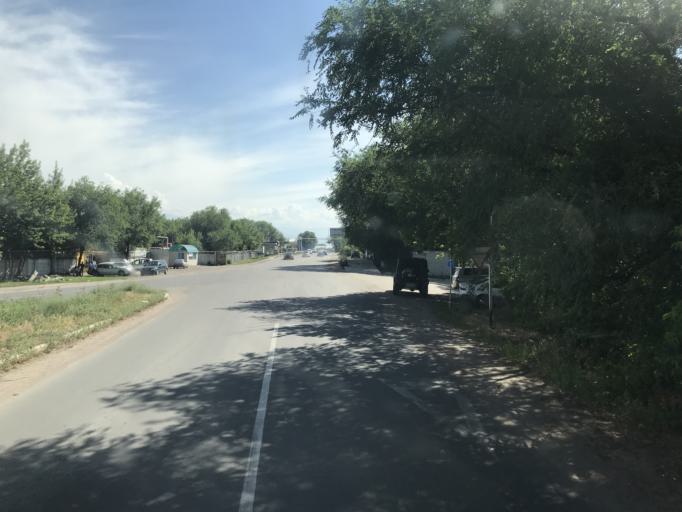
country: KZ
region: Almaty Oblysy
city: Pervomayskiy
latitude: 43.3503
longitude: 76.9050
